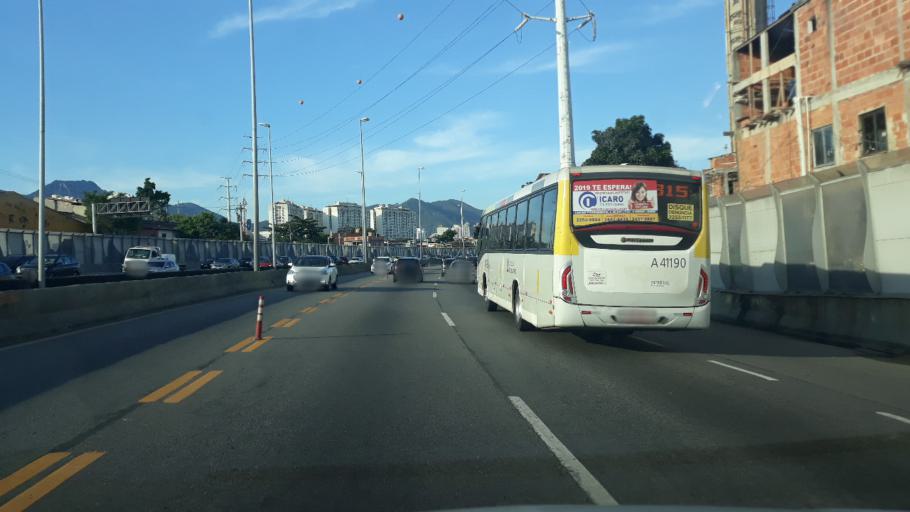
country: BR
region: Rio de Janeiro
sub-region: Rio De Janeiro
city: Rio de Janeiro
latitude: -22.8786
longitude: -43.2778
